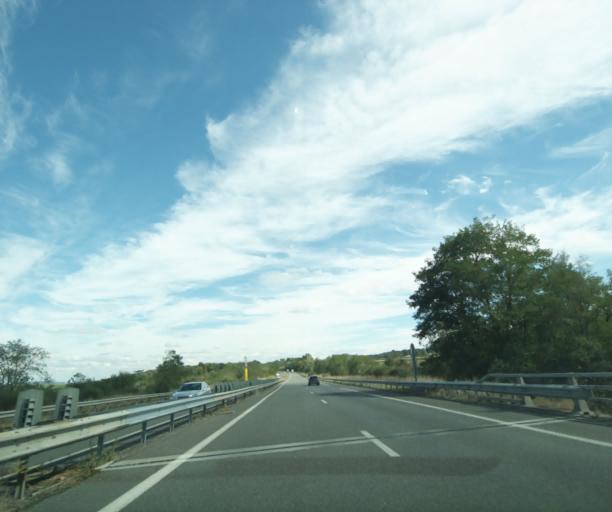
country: FR
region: Midi-Pyrenees
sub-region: Departement du Tarn-et-Garonne
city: Auvillar
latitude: 44.0582
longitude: 0.9192
